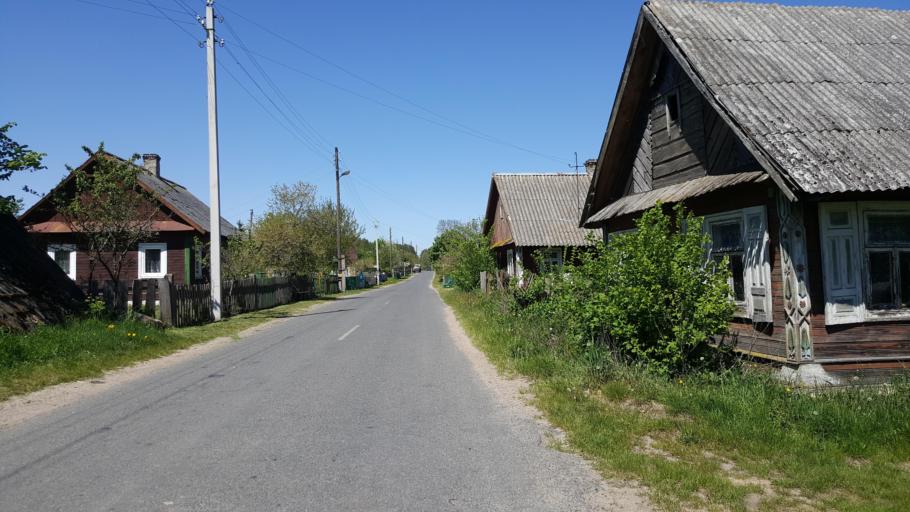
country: BY
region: Brest
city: Kamyanyuki
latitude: 52.5013
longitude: 23.7544
